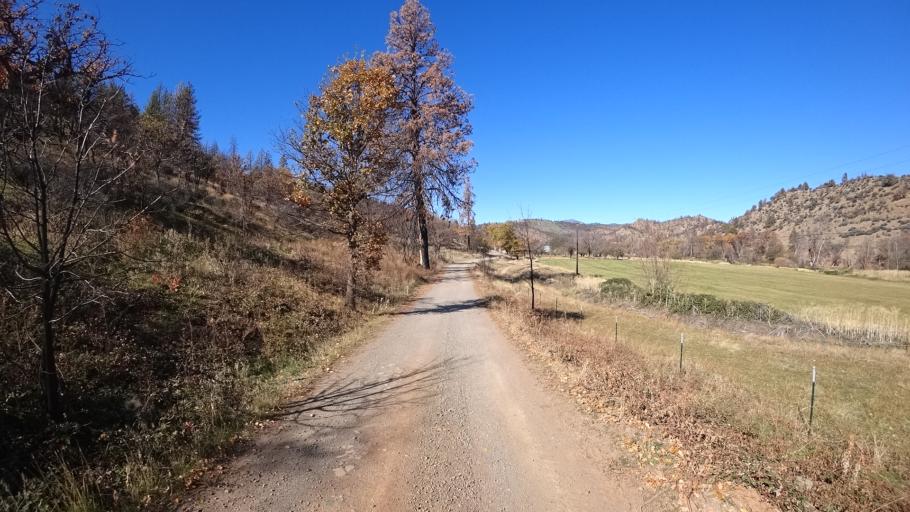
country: US
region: California
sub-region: Siskiyou County
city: Yreka
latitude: 41.9437
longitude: -122.5957
